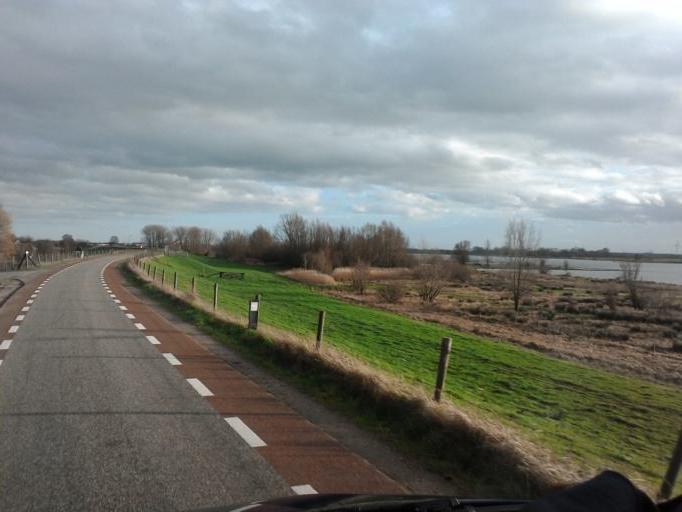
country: NL
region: Gelderland
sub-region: Gemeente Culemborg
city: Culemborg
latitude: 51.9702
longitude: 5.1797
